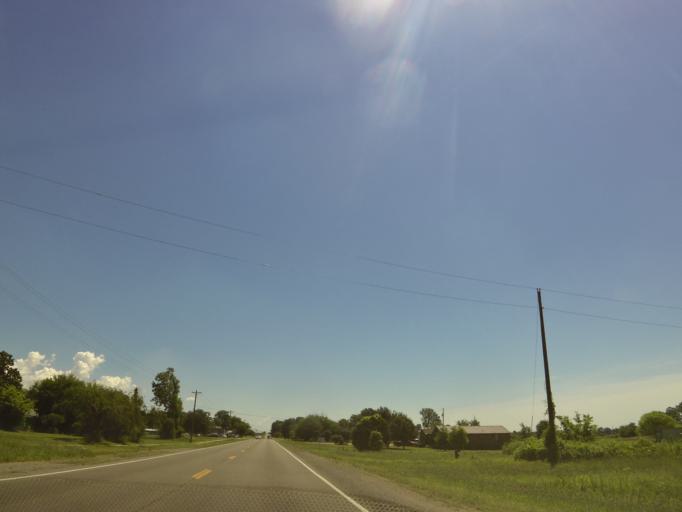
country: US
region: Missouri
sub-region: New Madrid County
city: Lilbourn
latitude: 36.5690
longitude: -89.5945
